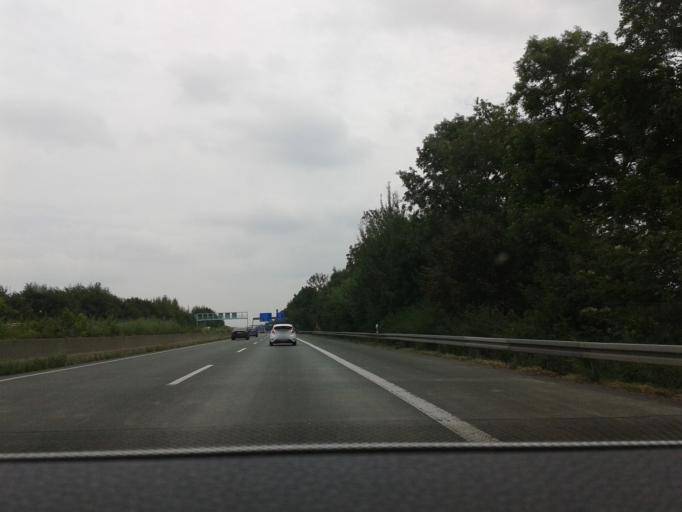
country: DE
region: North Rhine-Westphalia
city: Wickede
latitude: 51.5329
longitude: 7.8798
